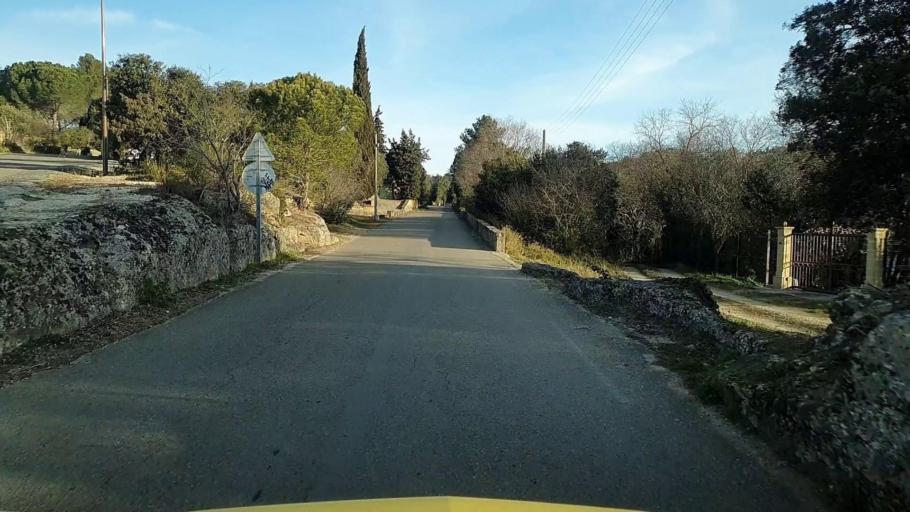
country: FR
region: Languedoc-Roussillon
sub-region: Departement du Gard
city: Castillon-du-Gard
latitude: 43.9608
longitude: 4.5527
